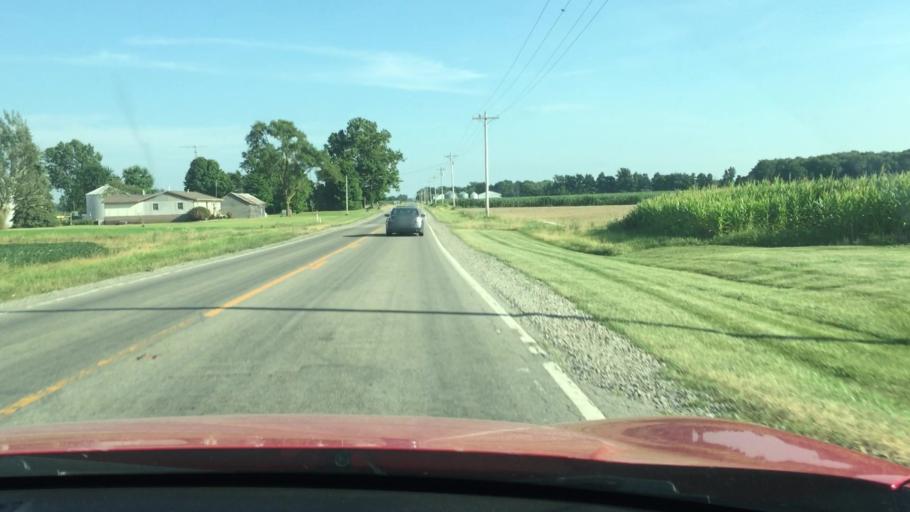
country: US
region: Ohio
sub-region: Hardin County
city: Ada
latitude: 40.6647
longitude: -83.8527
